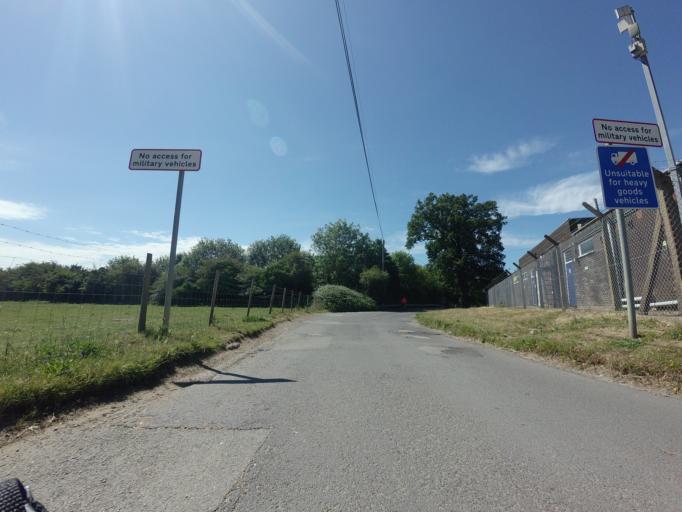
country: GB
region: England
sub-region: Kent
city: Strood
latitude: 51.4168
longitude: 0.5111
